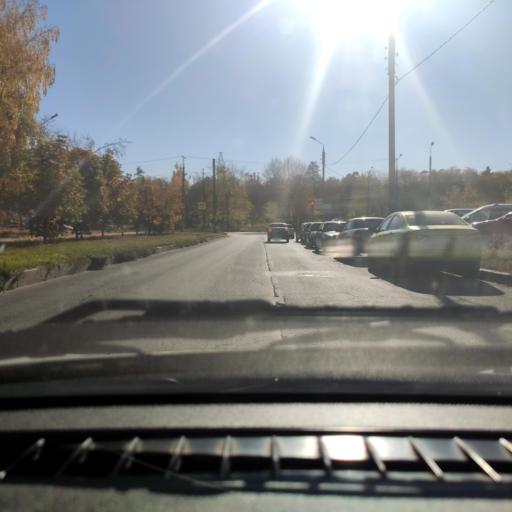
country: RU
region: Samara
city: Tol'yatti
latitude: 53.4995
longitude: 49.4017
